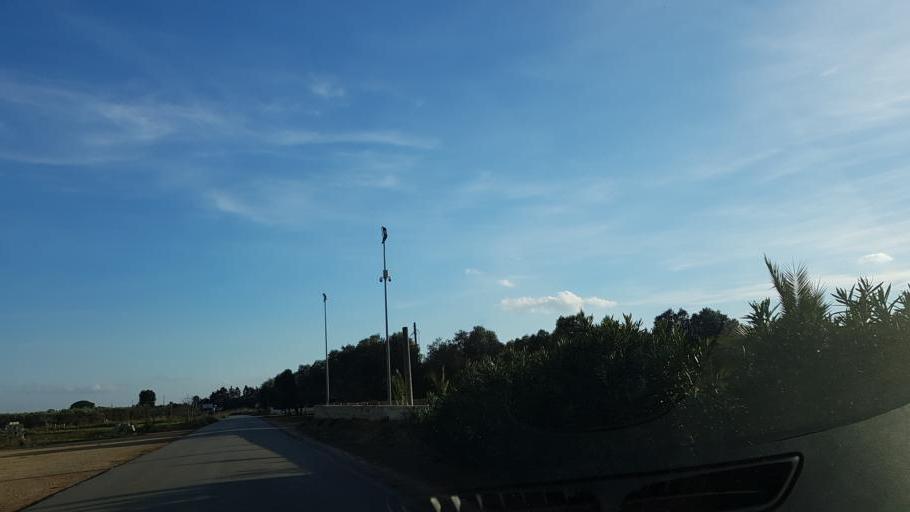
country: IT
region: Apulia
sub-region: Provincia di Brindisi
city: San Vito dei Normanni
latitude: 40.6869
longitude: 17.7653
